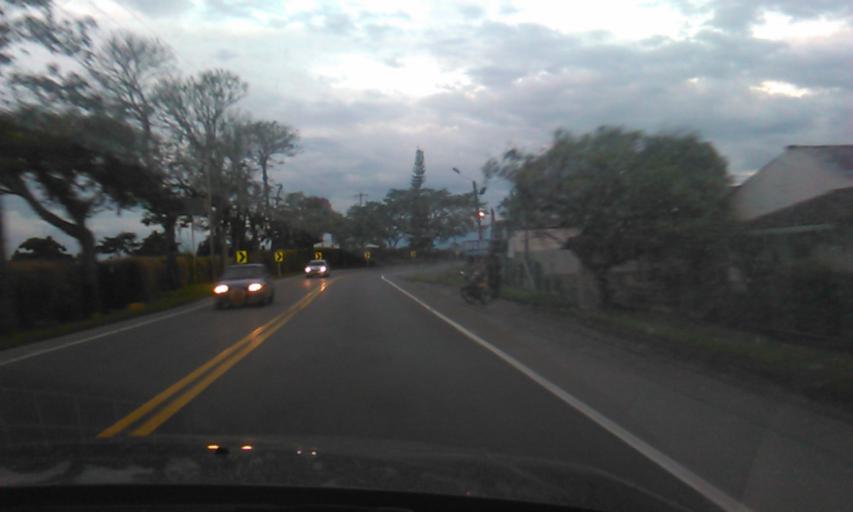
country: CO
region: Quindio
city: La Tebaida
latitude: 4.4506
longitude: -75.8041
